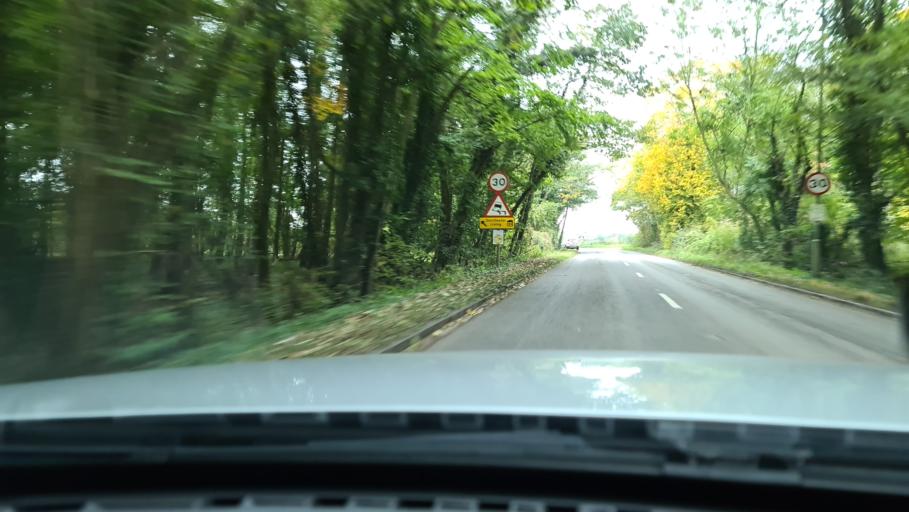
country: GB
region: England
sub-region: Oxfordshire
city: Somerton
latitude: 51.9263
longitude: -1.2419
